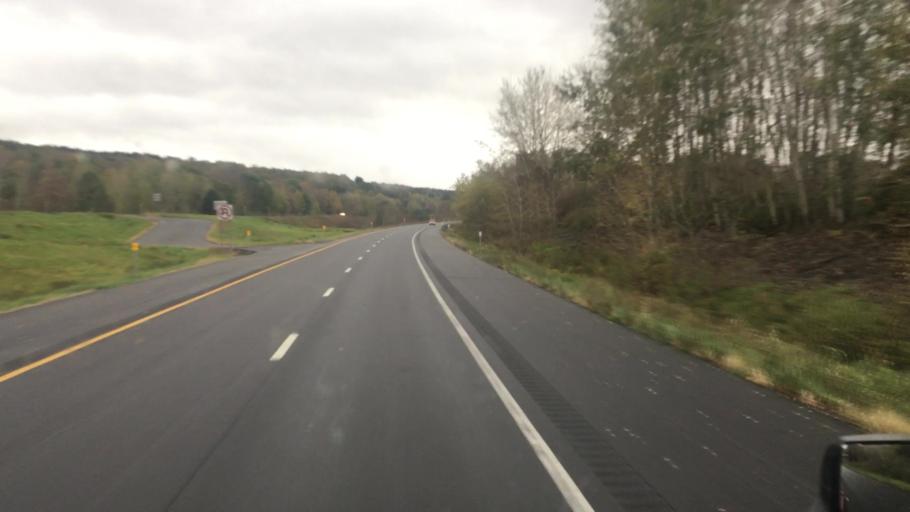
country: US
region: New York
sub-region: Chenango County
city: Bainbridge
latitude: 42.2123
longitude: -75.5165
